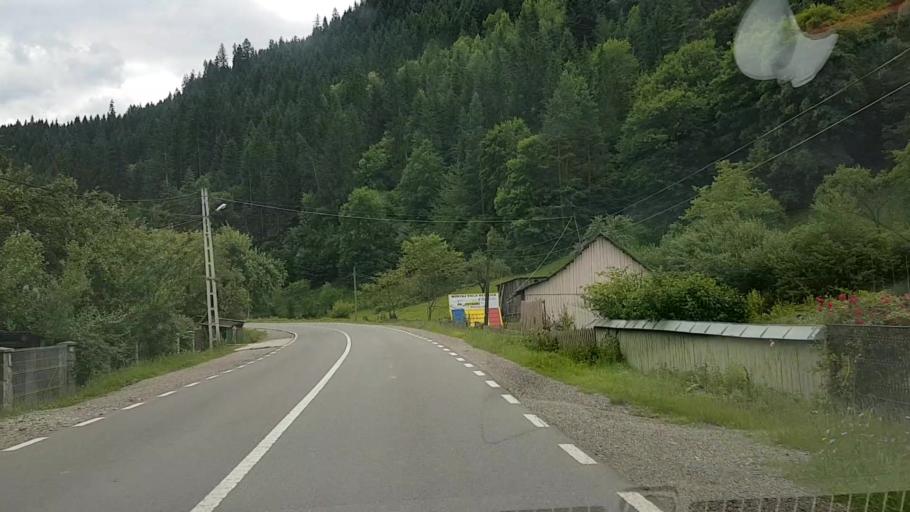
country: RO
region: Neamt
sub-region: Comuna Poiana Teiului
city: Poiana Teiului
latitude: 47.1088
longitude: 25.9316
